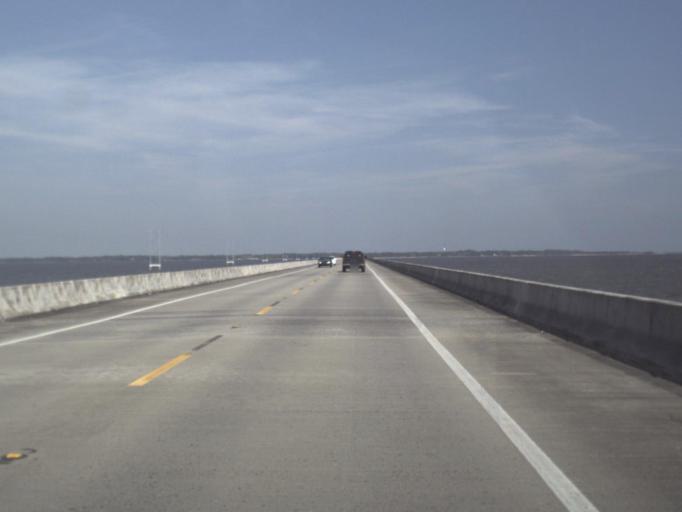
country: US
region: Florida
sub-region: Franklin County
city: Apalachicola
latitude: 29.7295
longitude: -84.9443
